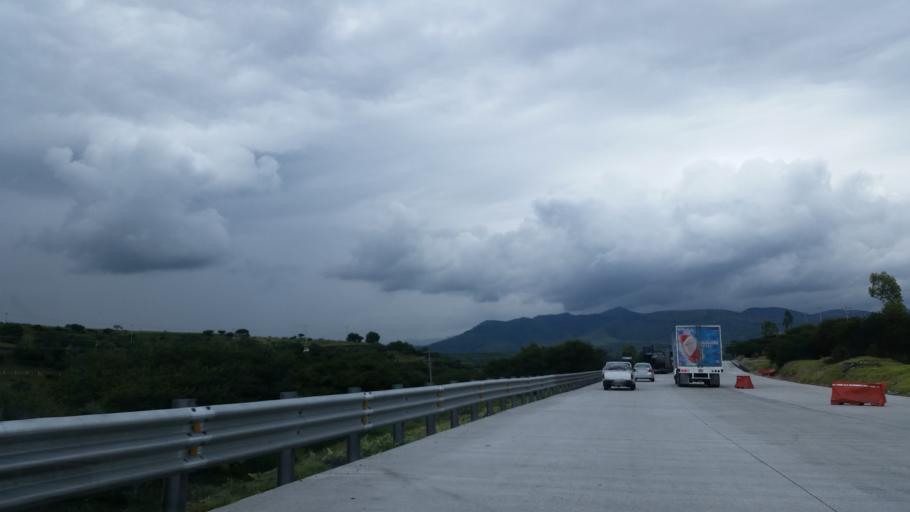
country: MX
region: Hidalgo
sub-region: Tepeji del Rio de Ocampo
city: Cantera de Villagran
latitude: 19.8637
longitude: -99.3171
